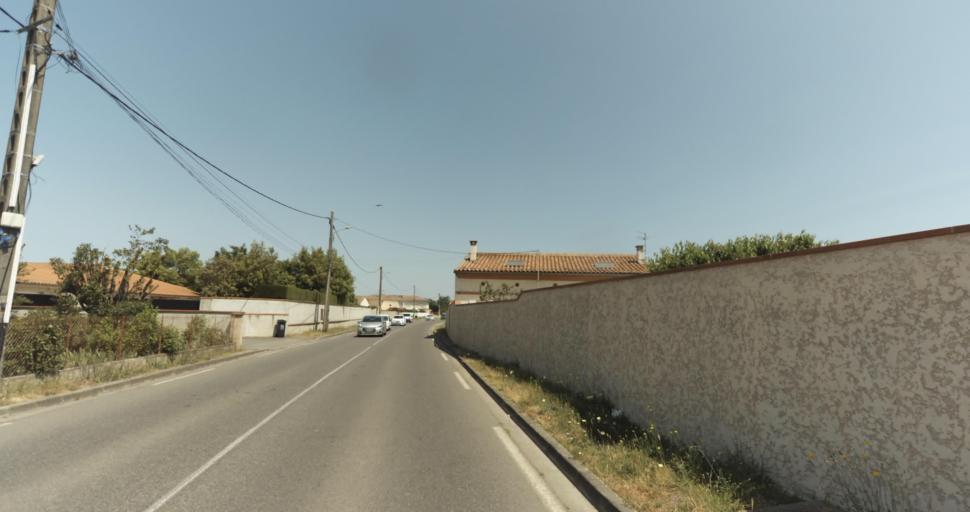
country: FR
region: Midi-Pyrenees
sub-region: Departement de la Haute-Garonne
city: La Salvetat-Saint-Gilles
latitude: 43.5653
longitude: 1.2657
